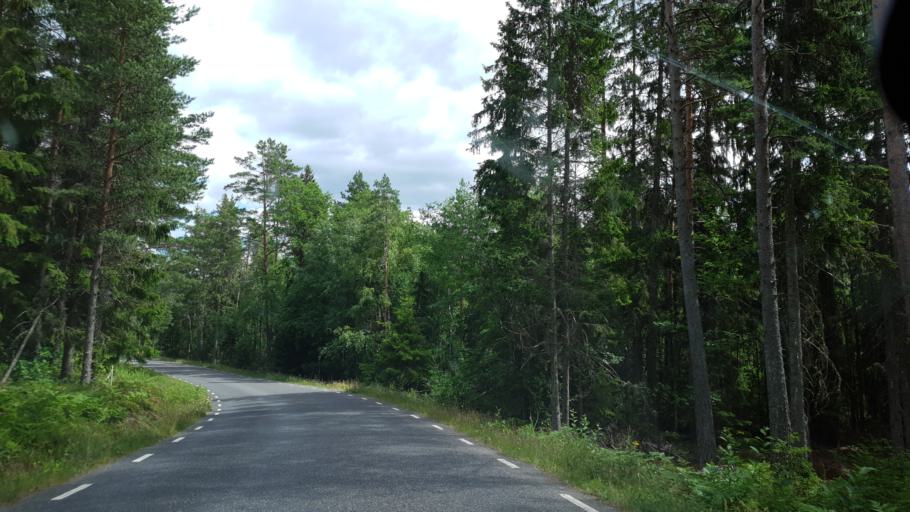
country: SE
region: Kronoberg
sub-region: Uppvidinge Kommun
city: Aseda
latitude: 57.1916
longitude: 15.4062
